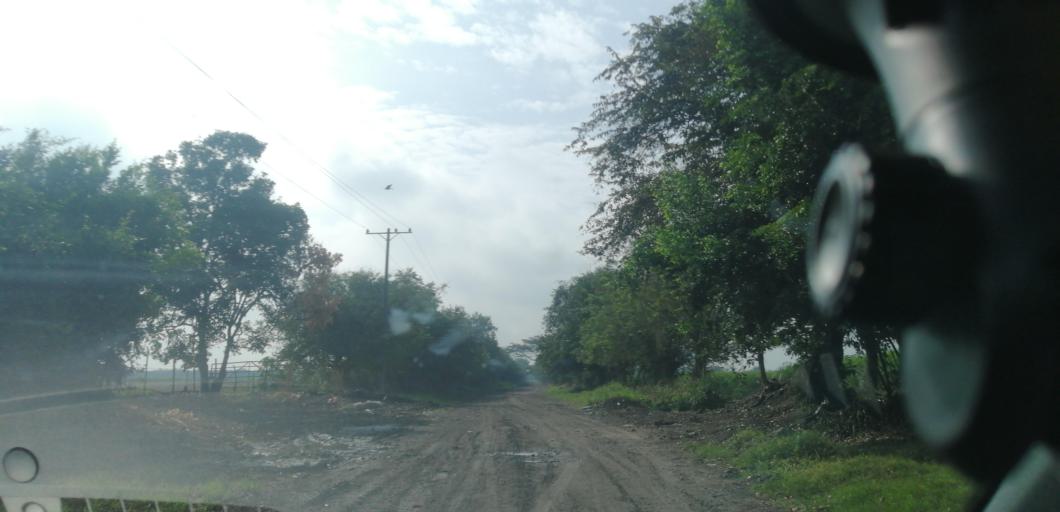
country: CO
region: Valle del Cauca
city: Palmira
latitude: 3.5491
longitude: -76.3626
